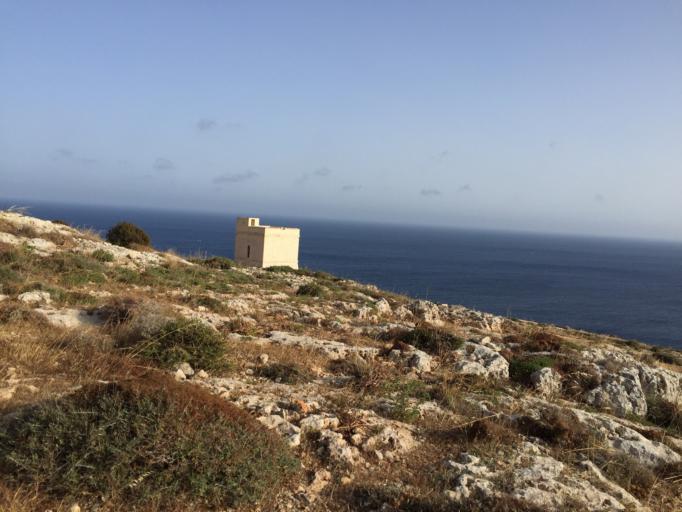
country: MT
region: Il-Qrendi
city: Qrendi
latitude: 35.8254
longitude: 14.4396
